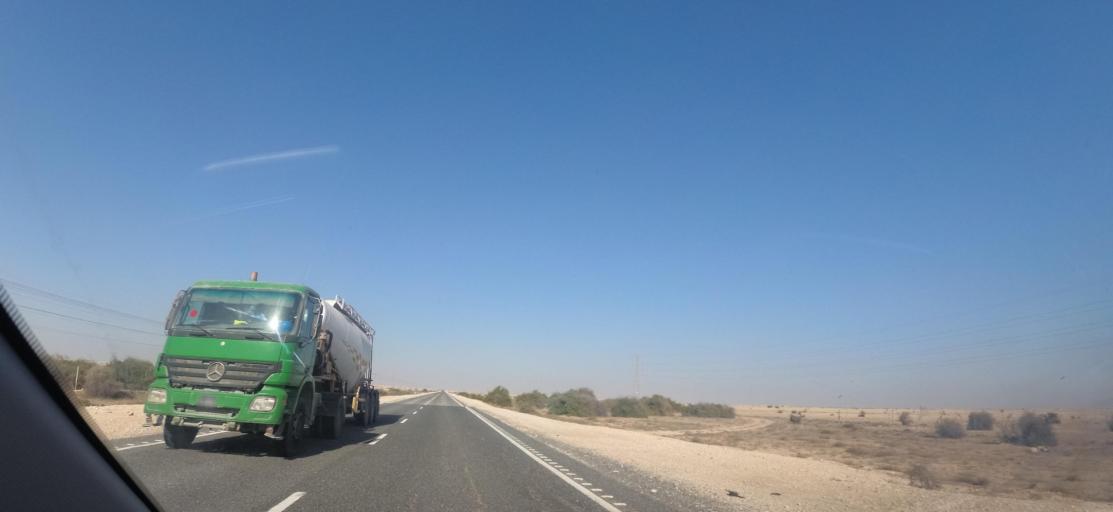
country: QA
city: Al Jumayliyah
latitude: 25.6729
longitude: 51.1299
